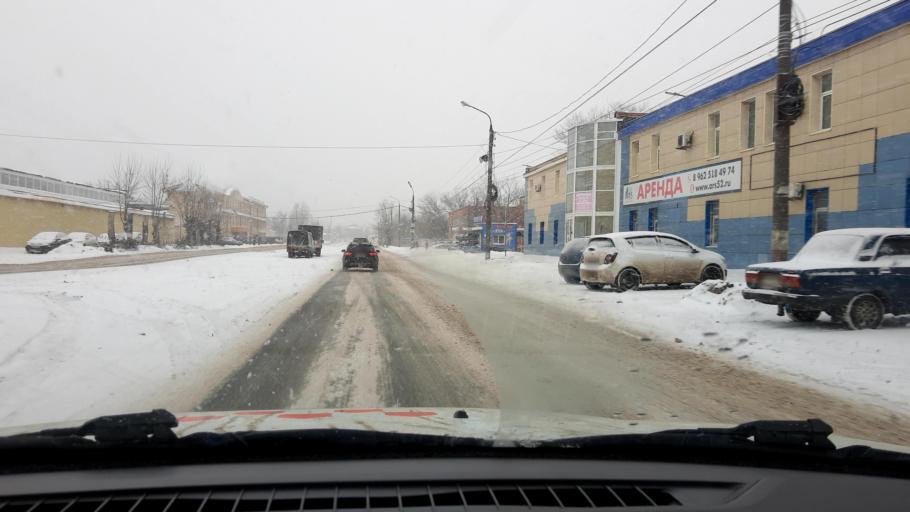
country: RU
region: Nizjnij Novgorod
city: Dzerzhinsk
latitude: 56.2410
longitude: 43.5010
